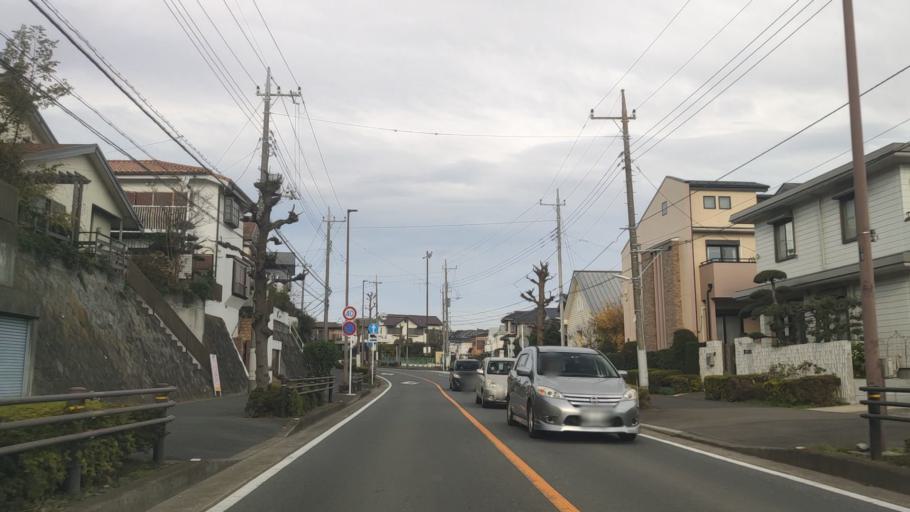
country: JP
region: Kanagawa
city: Atsugi
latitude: 35.4408
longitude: 139.4025
